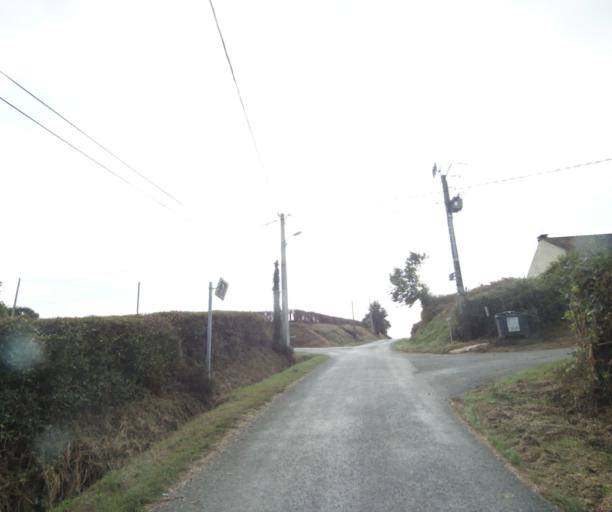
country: FR
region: Bourgogne
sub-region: Departement de Saone-et-Loire
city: Palinges
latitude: 46.4901
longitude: 4.2114
